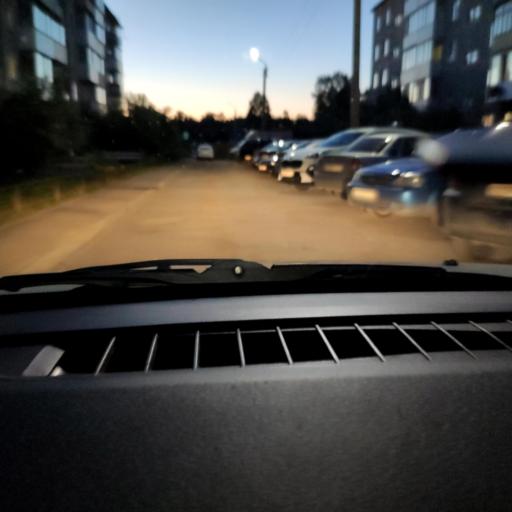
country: RU
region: Perm
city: Zvezdnyy
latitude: 57.7383
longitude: 56.3183
